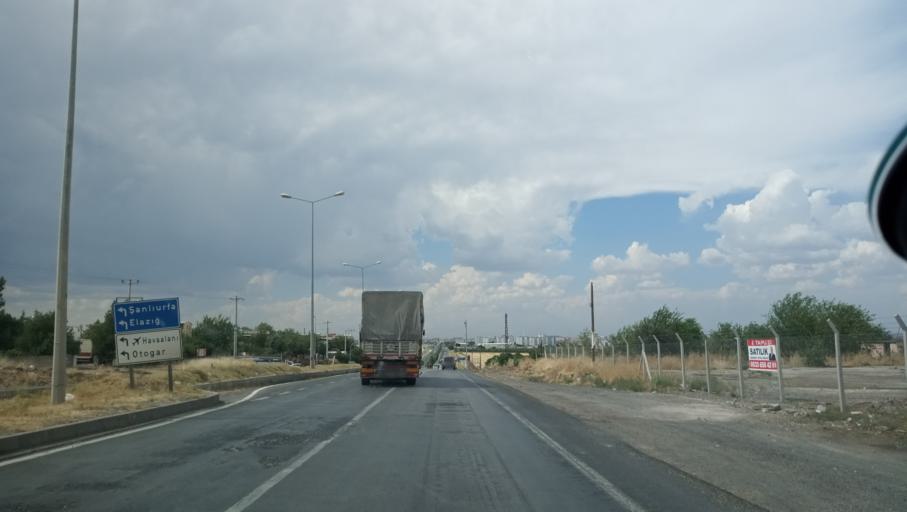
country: TR
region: Diyarbakir
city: Diyarbakir
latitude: 37.8726
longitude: 40.2214
